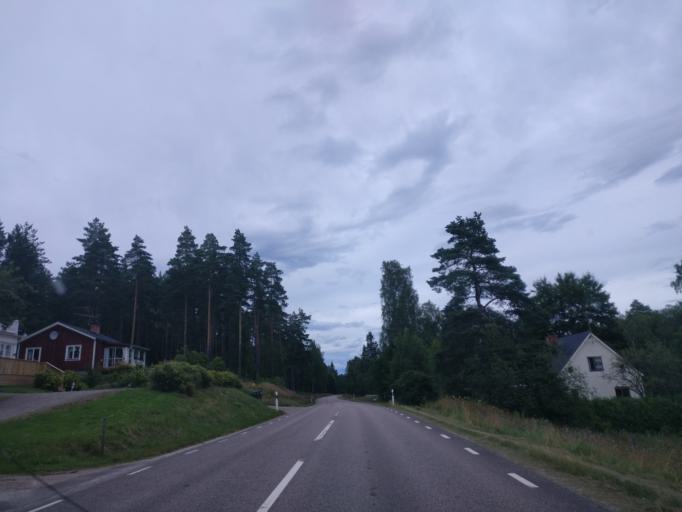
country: SE
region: Vaermland
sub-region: Hagfors Kommun
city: Ekshaerad
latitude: 60.1631
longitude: 13.4754
